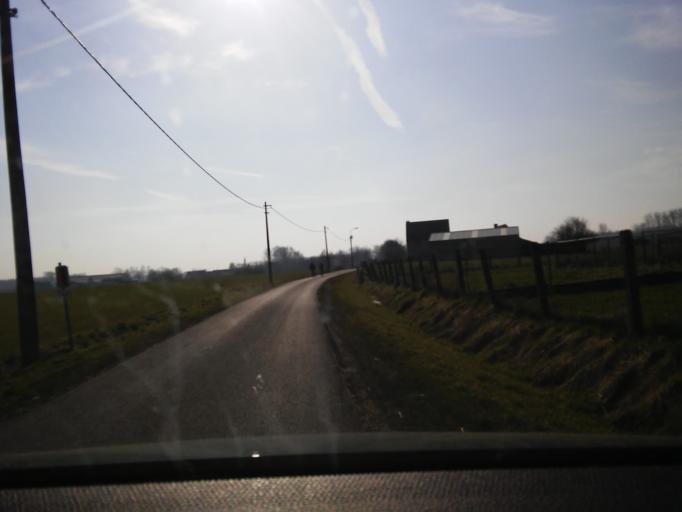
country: BE
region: Flanders
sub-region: Provincie Oost-Vlaanderen
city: Aalter
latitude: 51.0608
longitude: 3.4360
